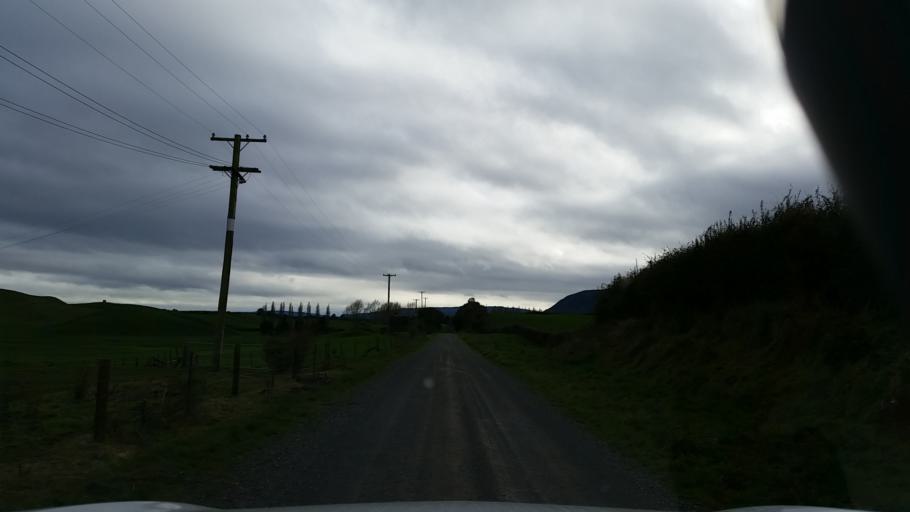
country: NZ
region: Bay of Plenty
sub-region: Whakatane District
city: Murupara
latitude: -38.3101
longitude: 176.4689
